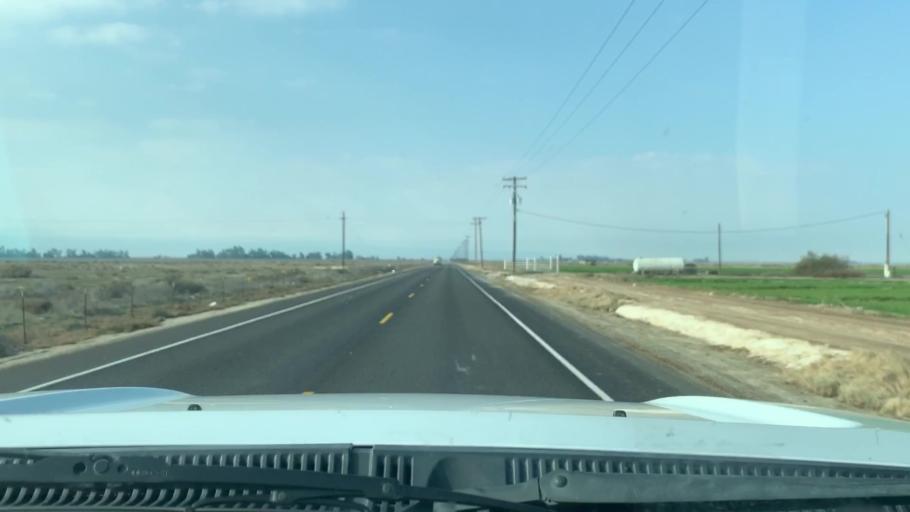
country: US
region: California
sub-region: Kern County
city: Buttonwillow
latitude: 35.4421
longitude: -119.3828
